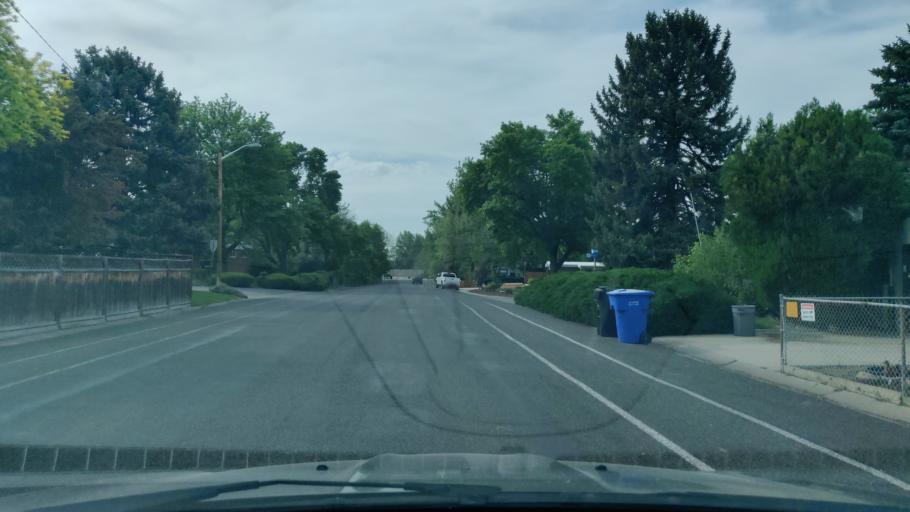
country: US
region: Utah
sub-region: Salt Lake County
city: Little Cottonwood Creek Valley
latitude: 40.6291
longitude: -111.8390
